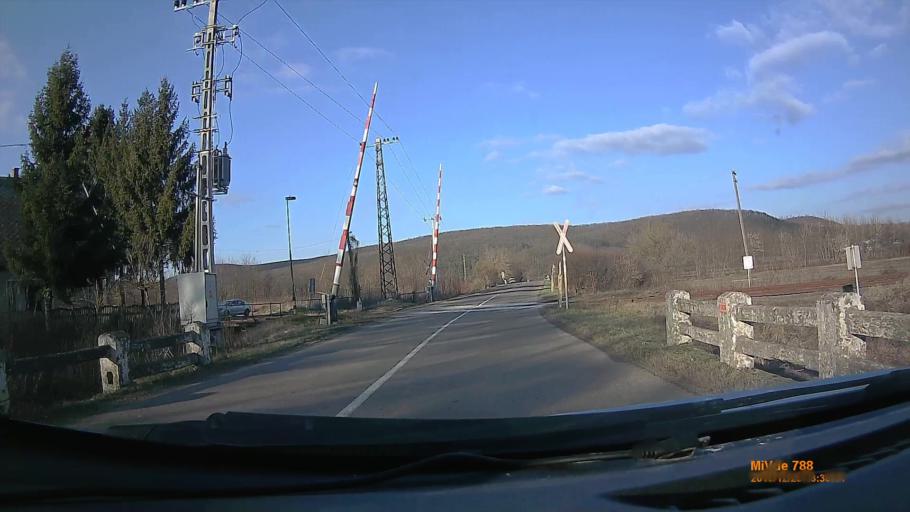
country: HU
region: Heves
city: Sirok
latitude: 47.9151
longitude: 20.1774
